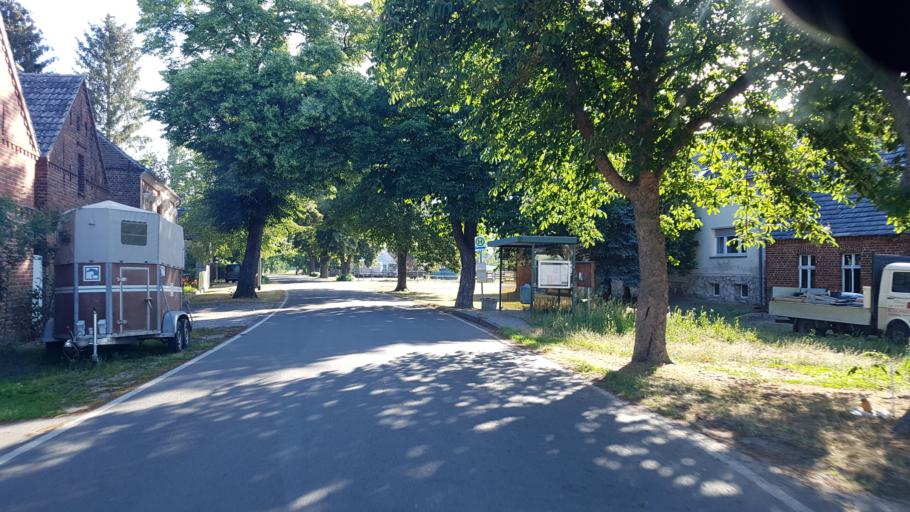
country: DE
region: Brandenburg
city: Kasel-Golzig
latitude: 51.9587
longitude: 13.6701
